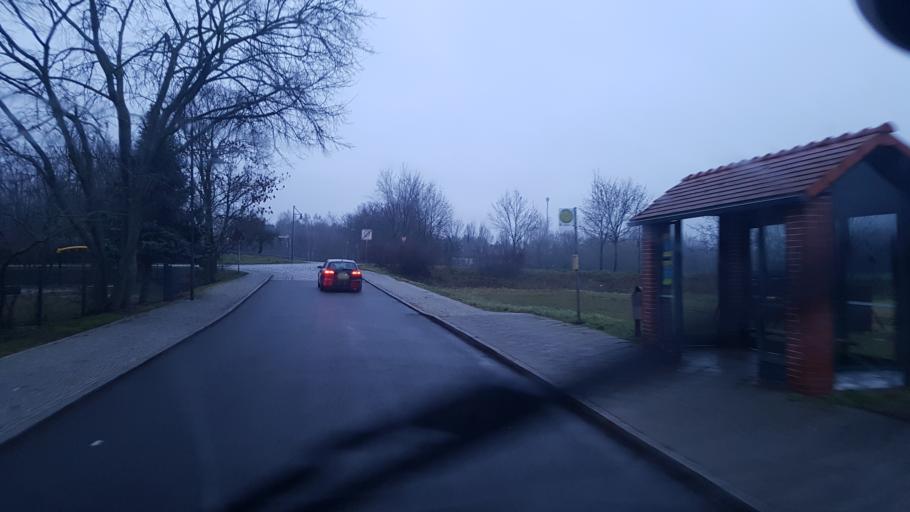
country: DE
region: Brandenburg
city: Ludwigsfelde
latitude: 52.3168
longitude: 13.2007
